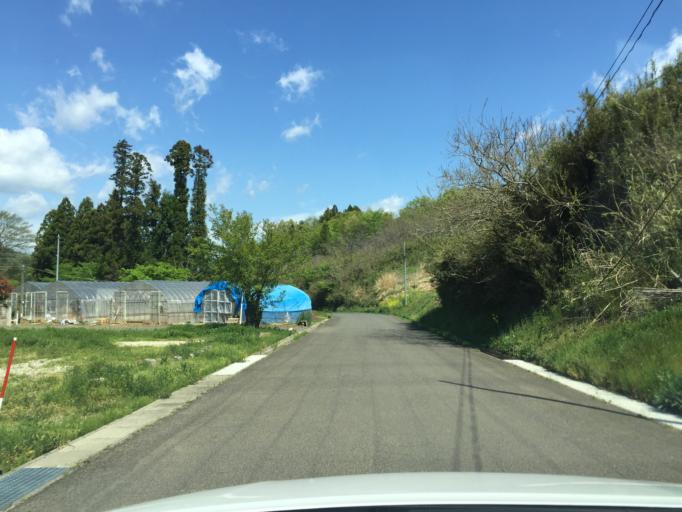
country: JP
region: Fukushima
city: Fukushima-shi
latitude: 37.6704
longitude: 140.4600
